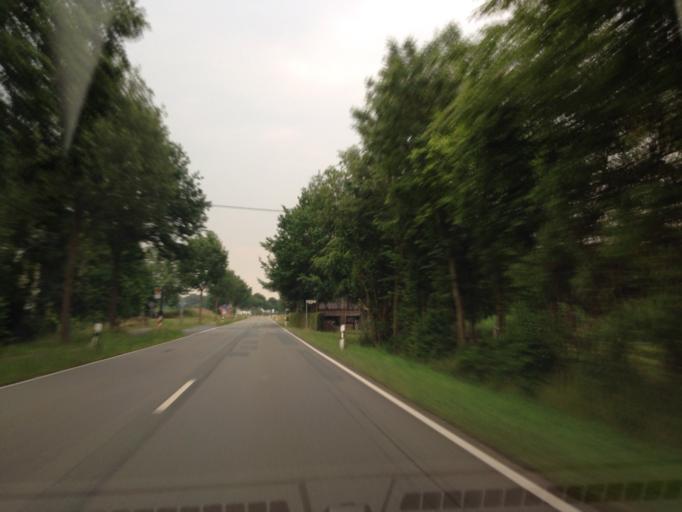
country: DE
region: North Rhine-Westphalia
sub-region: Regierungsbezirk Munster
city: Havixbeck
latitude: 51.9536
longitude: 7.4292
